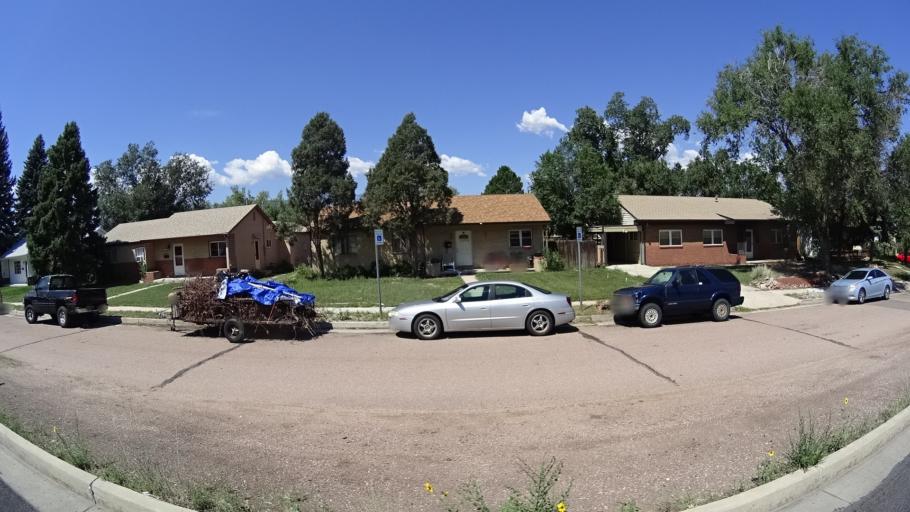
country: US
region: Colorado
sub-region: El Paso County
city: Colorado Springs
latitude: 38.8646
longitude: -104.7942
